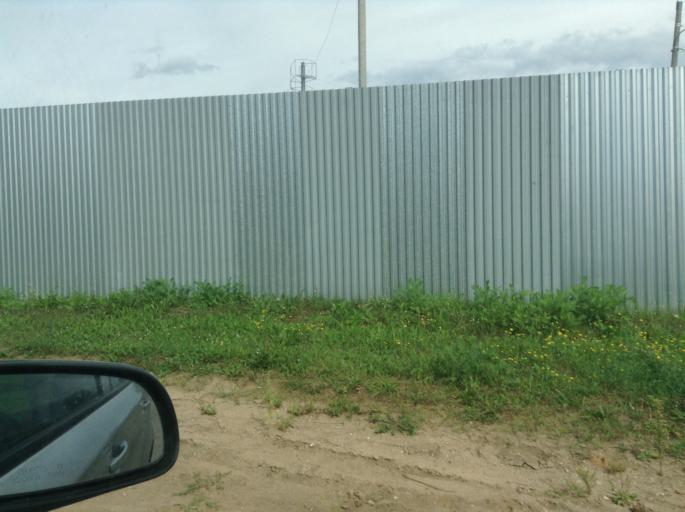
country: RU
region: Moskovskaya
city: Yegor'yevsk
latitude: 55.3645
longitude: 39.0966
